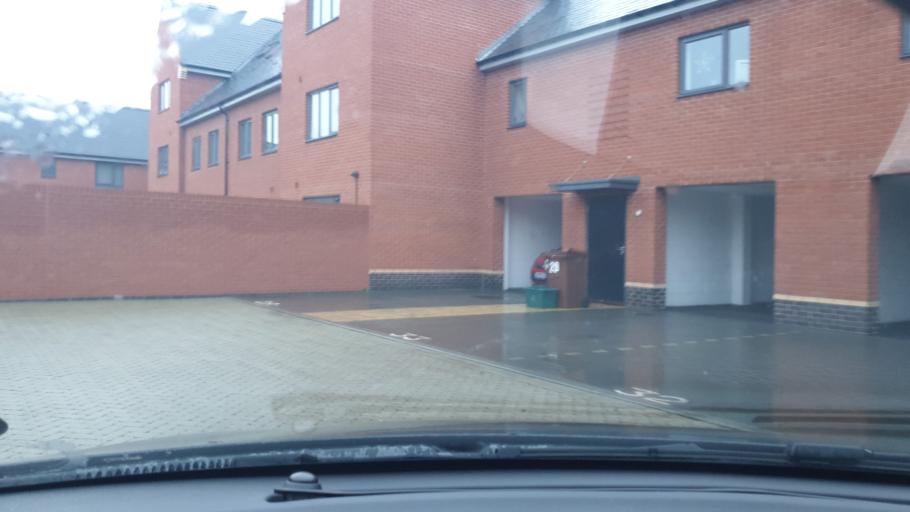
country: GB
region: England
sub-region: Essex
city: Colchester
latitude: 51.9173
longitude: 0.8990
